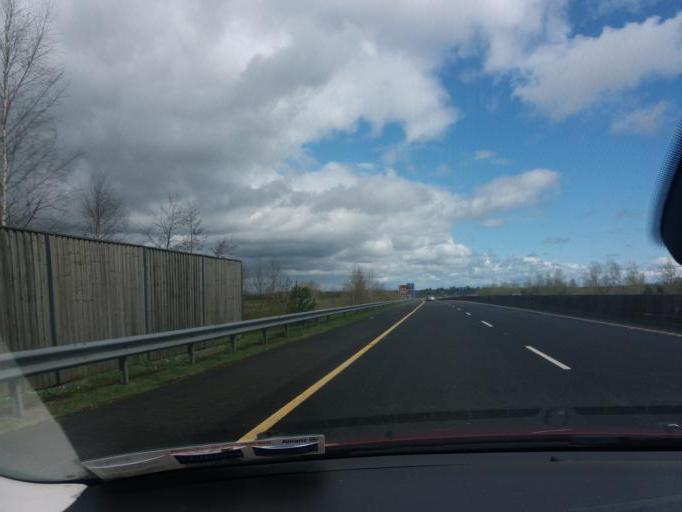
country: IE
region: Munster
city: Thurles
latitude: 52.6138
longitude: -7.7861
